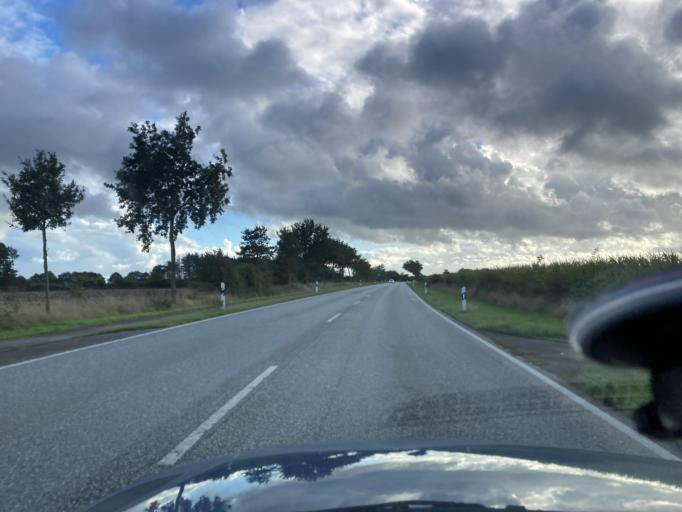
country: DE
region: Schleswig-Holstein
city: Hamdorf
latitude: 54.2444
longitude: 9.5285
